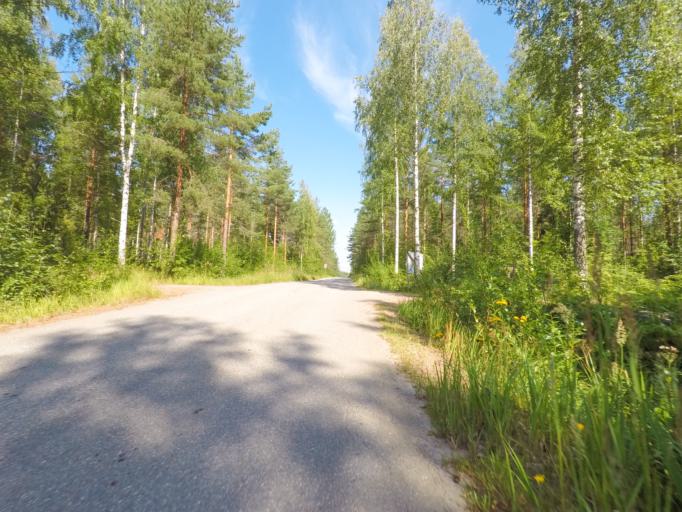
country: FI
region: Southern Savonia
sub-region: Mikkeli
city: Puumala
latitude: 61.4062
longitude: 28.0833
